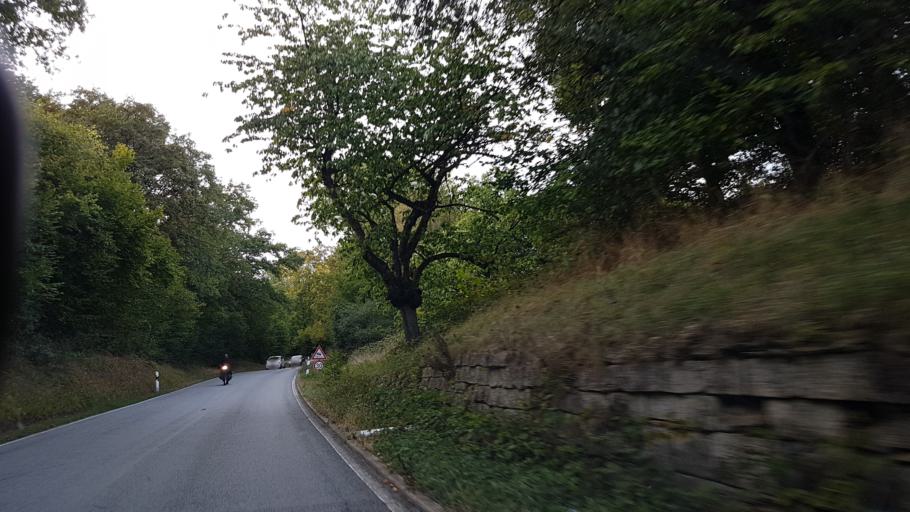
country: DE
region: Baden-Wuerttemberg
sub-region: Regierungsbezirk Stuttgart
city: Eberstadt
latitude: 49.1876
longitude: 9.3297
